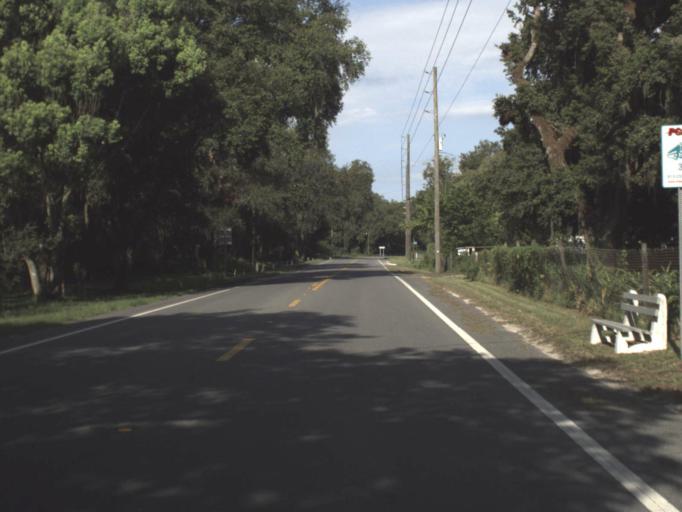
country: US
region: Florida
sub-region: Pasco County
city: Lacoochee
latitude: 28.4646
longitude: -82.1766
